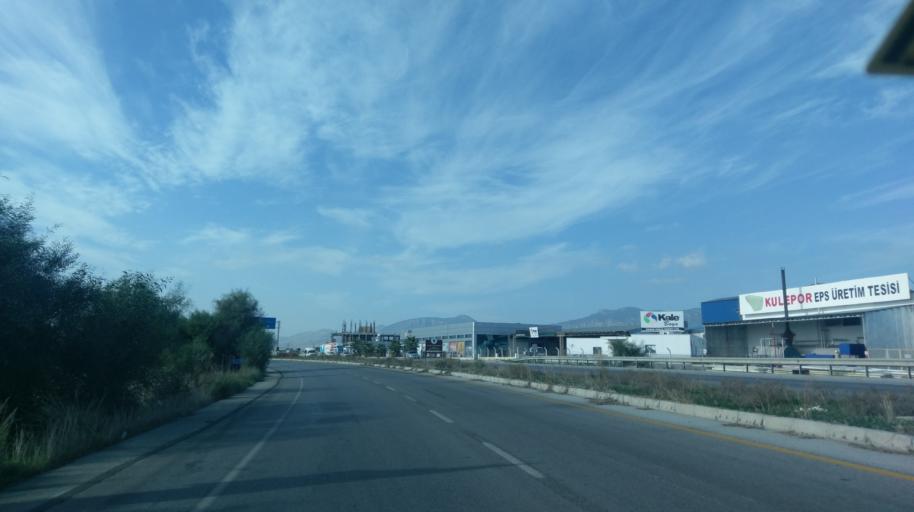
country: CY
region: Ammochostos
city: Lefkonoiko
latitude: 35.2065
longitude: 33.5956
